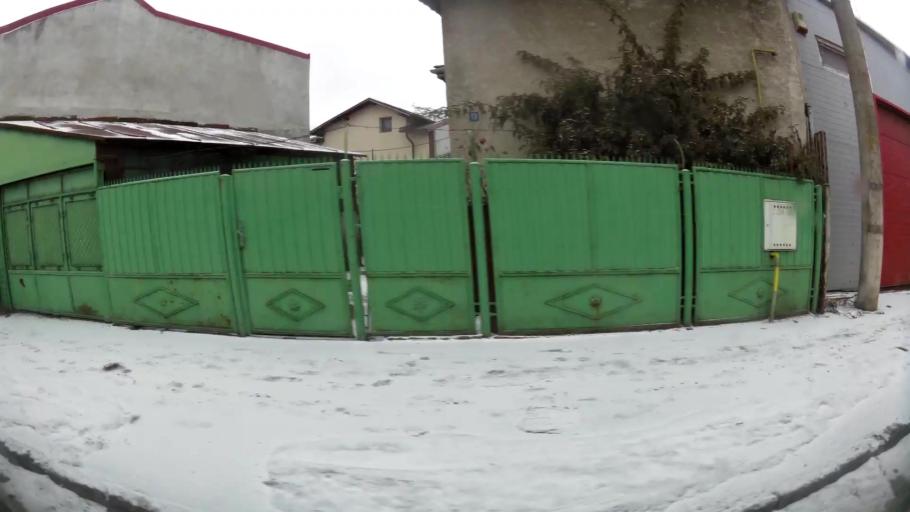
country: RO
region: Prahova
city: Ploiesti
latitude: 44.9508
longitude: 26.0187
